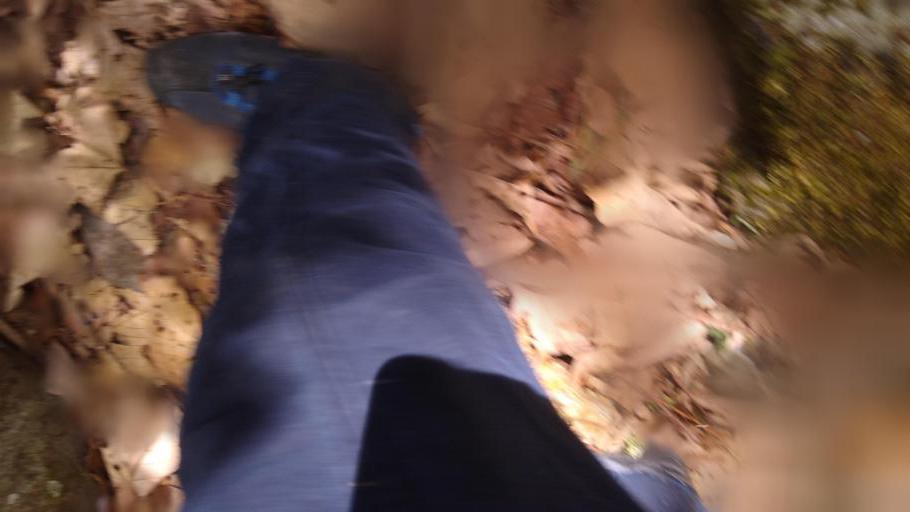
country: MX
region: Puebla
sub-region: Tepetzintla
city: Tlamanca de Hernandez
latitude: 19.9343
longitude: -97.8159
